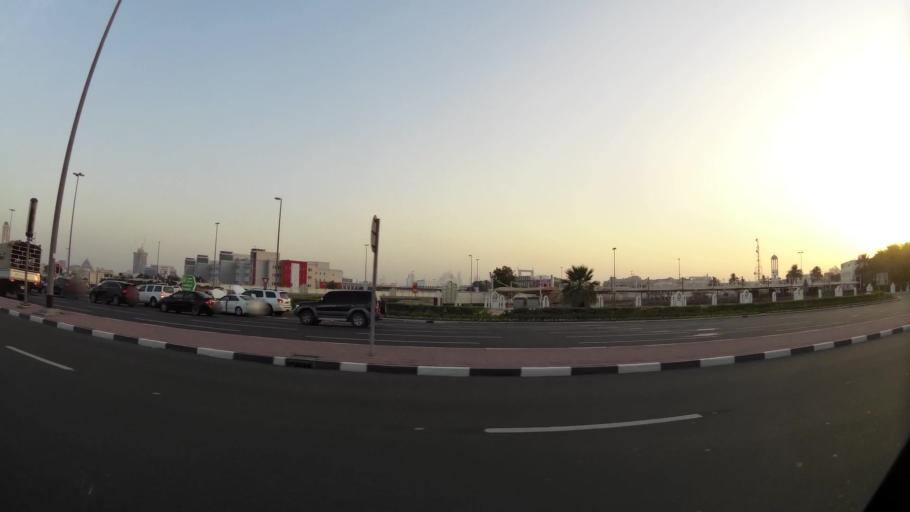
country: AE
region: Ash Shariqah
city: Sharjah
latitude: 25.2466
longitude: 55.3214
